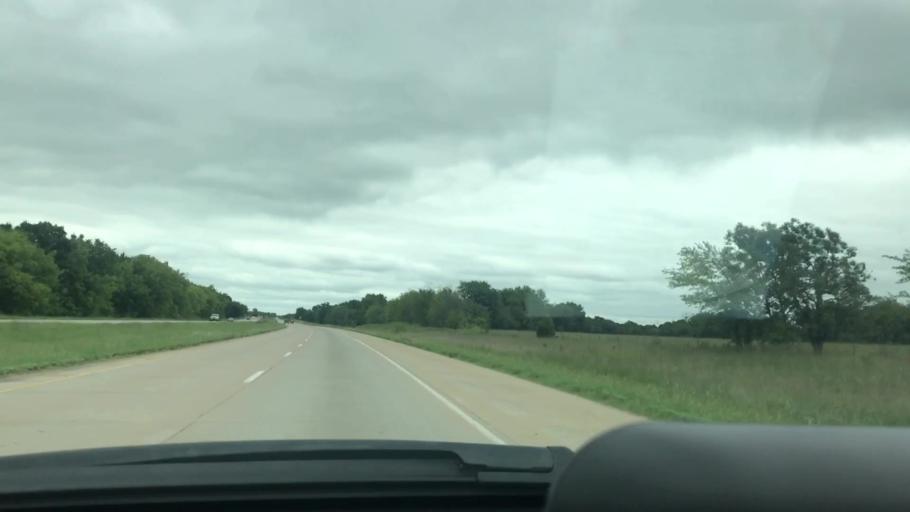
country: US
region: Oklahoma
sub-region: Mayes County
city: Chouteau
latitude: 36.2006
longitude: -95.3408
